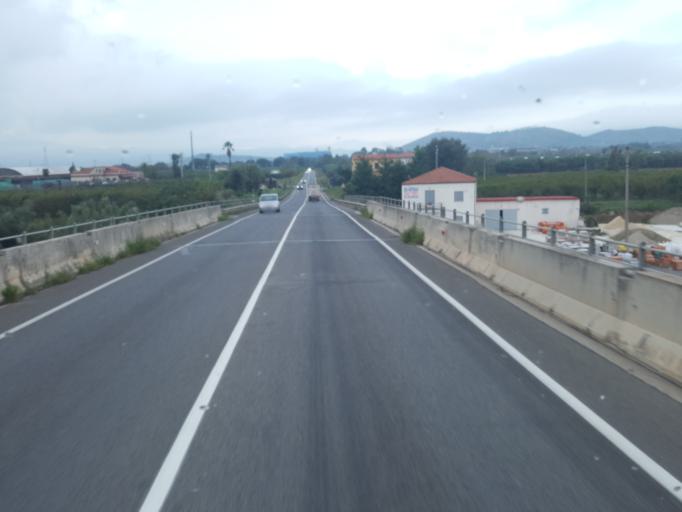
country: IT
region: Campania
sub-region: Provincia di Caserta
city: Pignataro Maggiore
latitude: 41.1725
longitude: 14.1351
